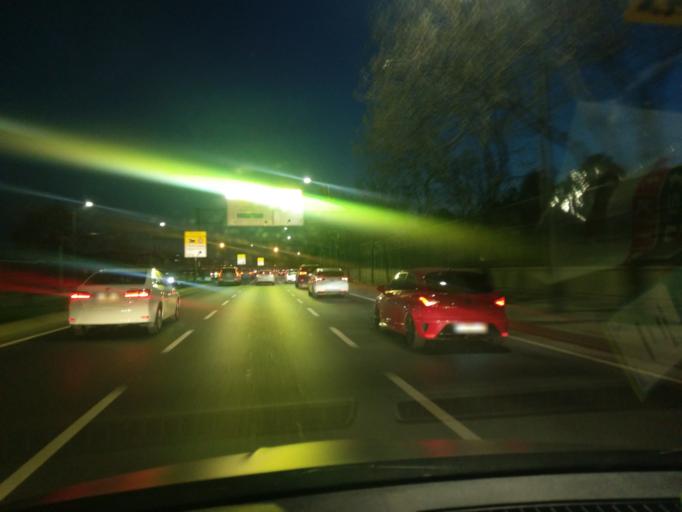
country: TR
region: Istanbul
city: Bahcelievler
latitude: 40.9716
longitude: 28.8449
